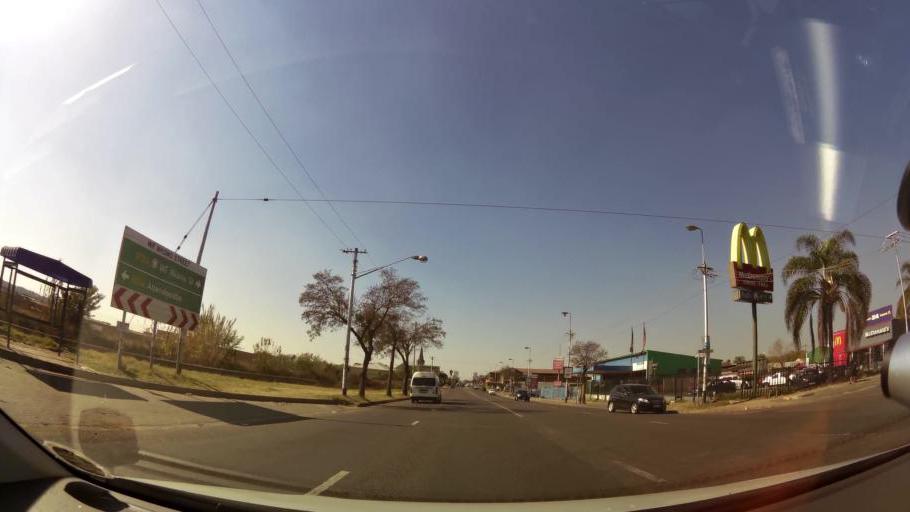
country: ZA
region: Gauteng
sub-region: City of Tshwane Metropolitan Municipality
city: Pretoria
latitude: -25.7492
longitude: 28.1472
